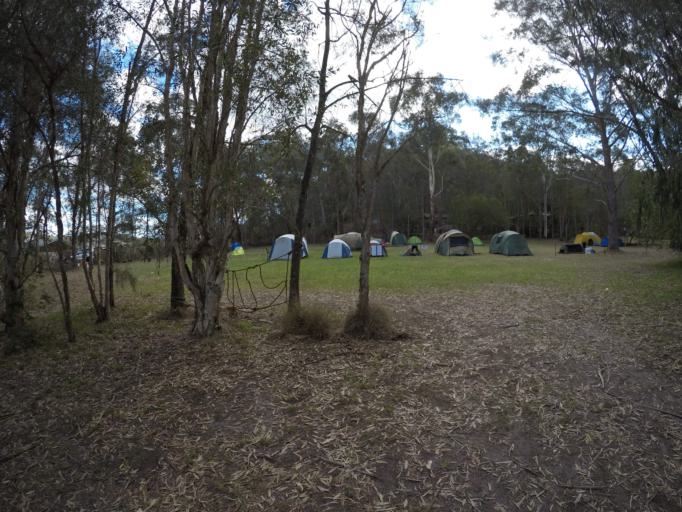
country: AU
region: New South Wales
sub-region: Hawkesbury
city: Pitt Town
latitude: -33.4706
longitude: 150.8912
